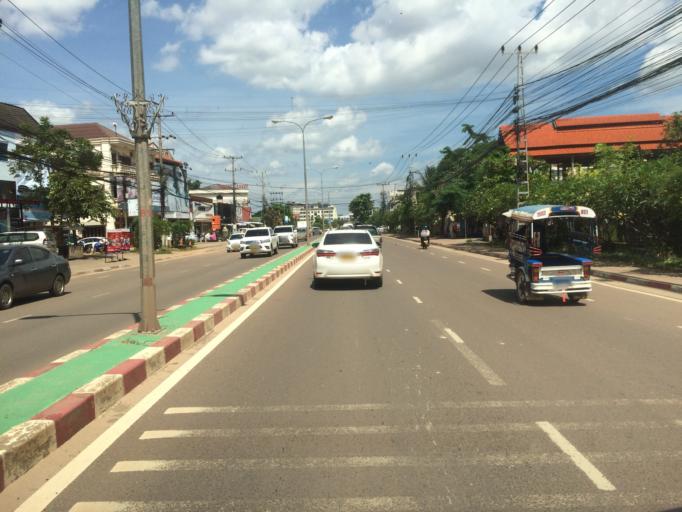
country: LA
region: Vientiane
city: Vientiane
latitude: 17.9686
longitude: 102.5921
